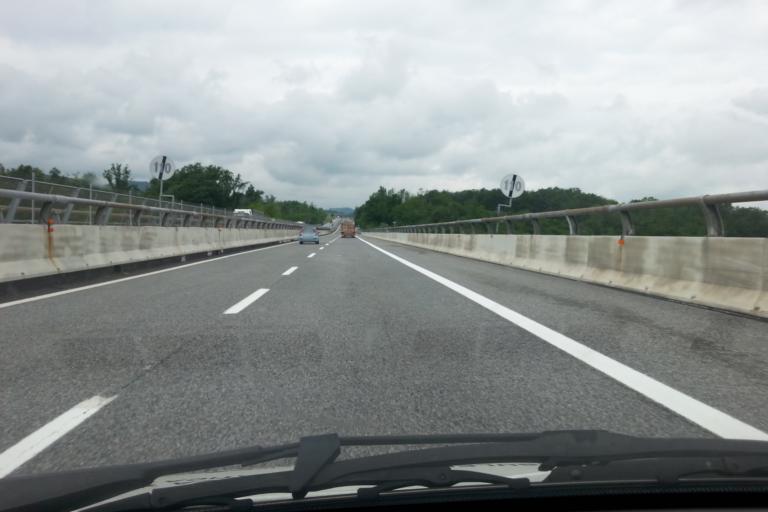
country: IT
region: Piedmont
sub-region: Provincia di Cuneo
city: Lesegno
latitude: 44.4112
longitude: 7.9562
